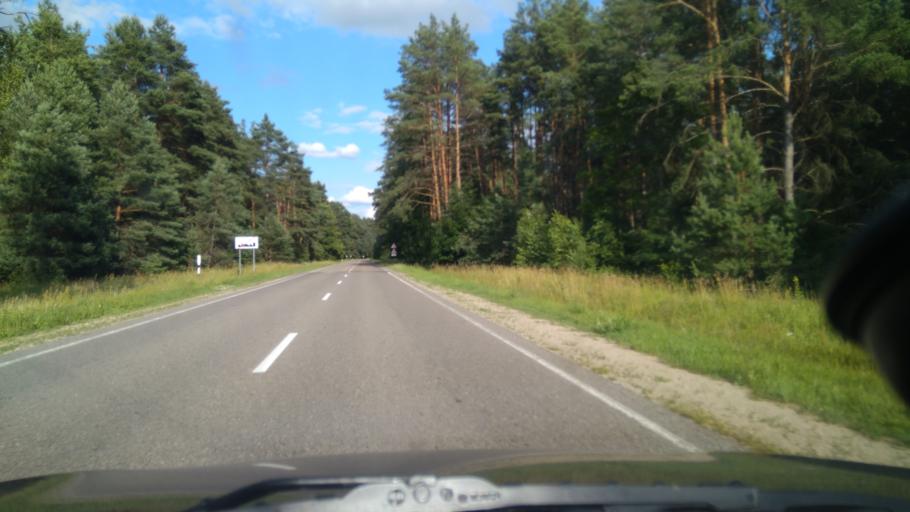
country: BY
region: Grodnenskaya
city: Masty
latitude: 53.3488
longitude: 24.6470
